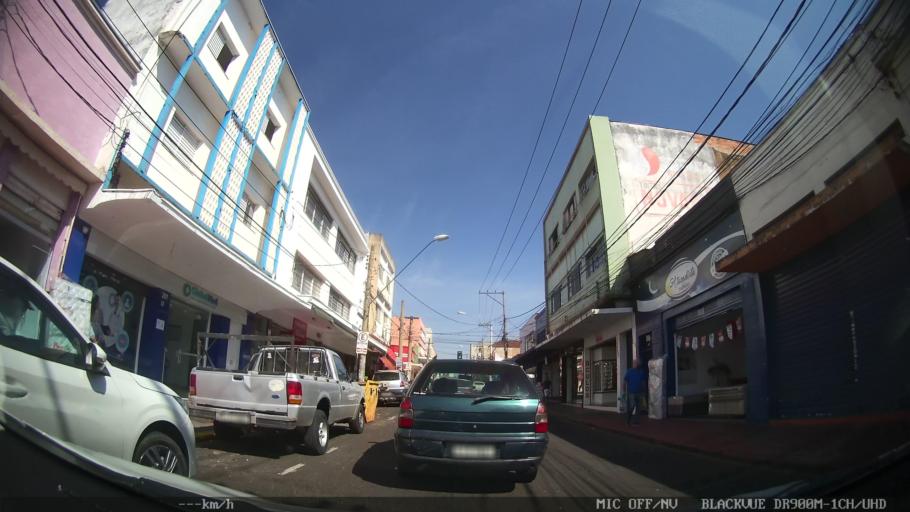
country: BR
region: Sao Paulo
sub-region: Ribeirao Preto
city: Ribeirao Preto
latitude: -21.1726
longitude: -47.8103
